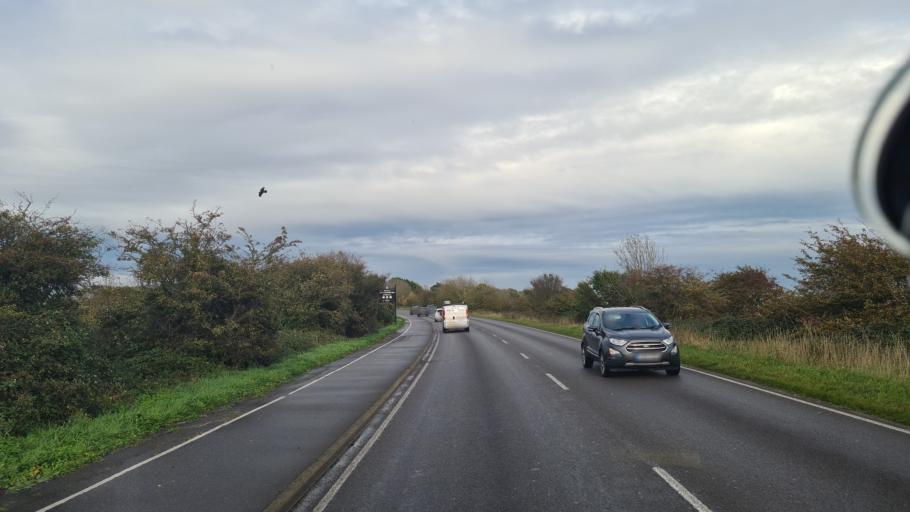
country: GB
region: England
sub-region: West Sussex
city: Littlehampton
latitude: 50.8090
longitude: -0.5647
